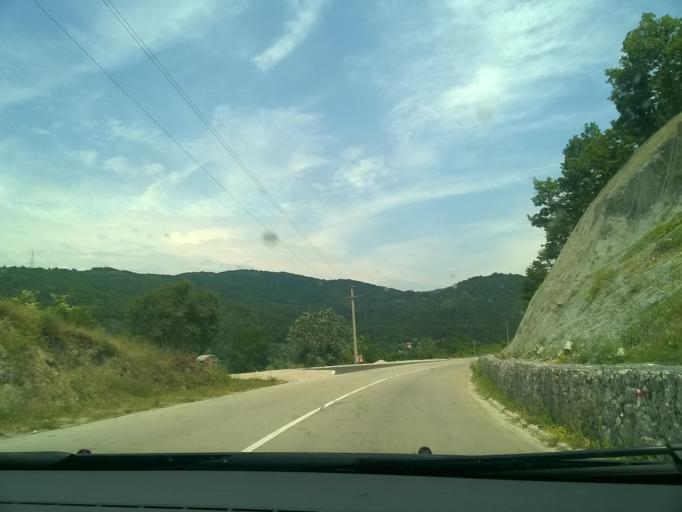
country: RS
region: Central Serbia
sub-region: Nisavski Okrug
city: Aleksinac
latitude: 43.6478
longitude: 21.7127
